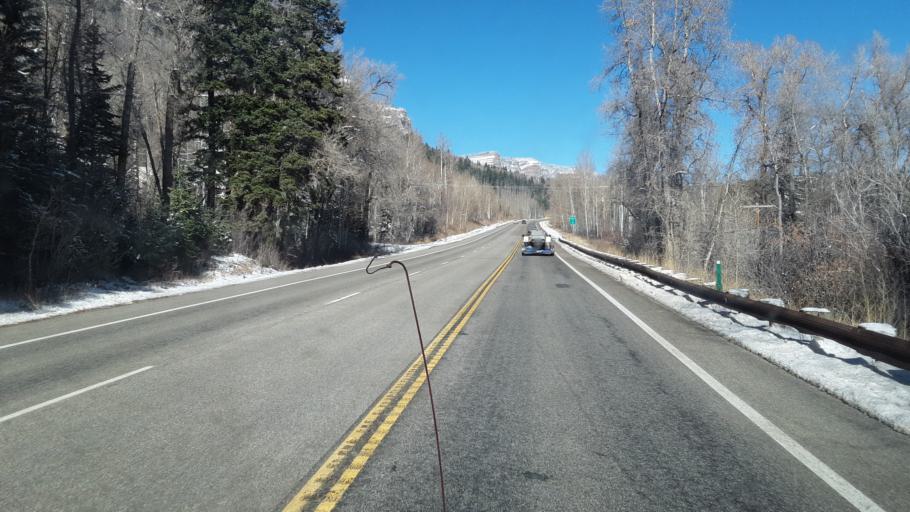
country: US
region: Colorado
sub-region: La Plata County
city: Durango
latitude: 37.5496
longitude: -107.8242
